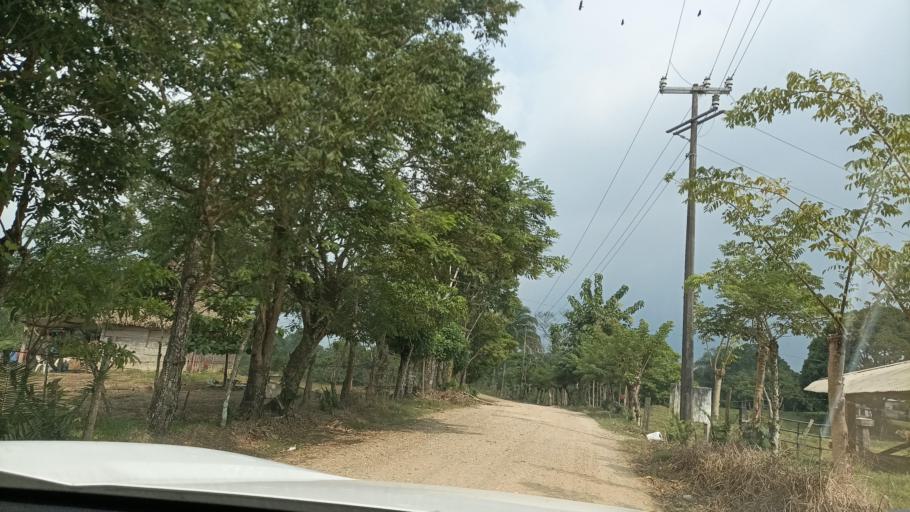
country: MX
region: Tabasco
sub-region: Huimanguillo
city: Francisco Rueda
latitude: 17.5885
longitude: -94.2004
